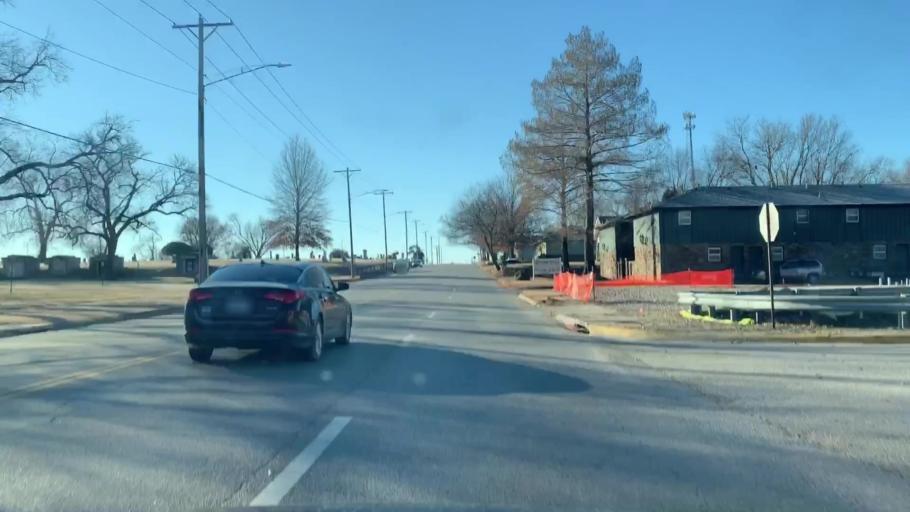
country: US
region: Kansas
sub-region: Crawford County
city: Pittsburg
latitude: 37.3862
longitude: -94.7053
